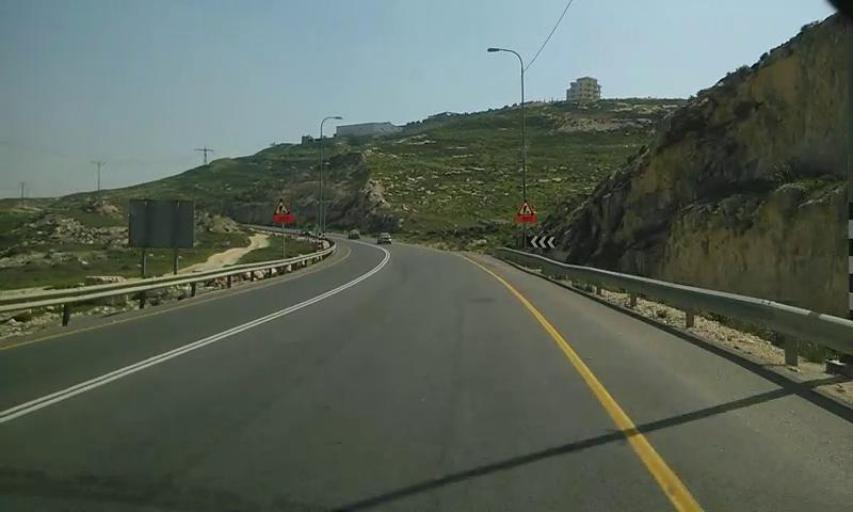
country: PS
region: West Bank
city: Jaba`
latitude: 31.8621
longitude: 35.2606
